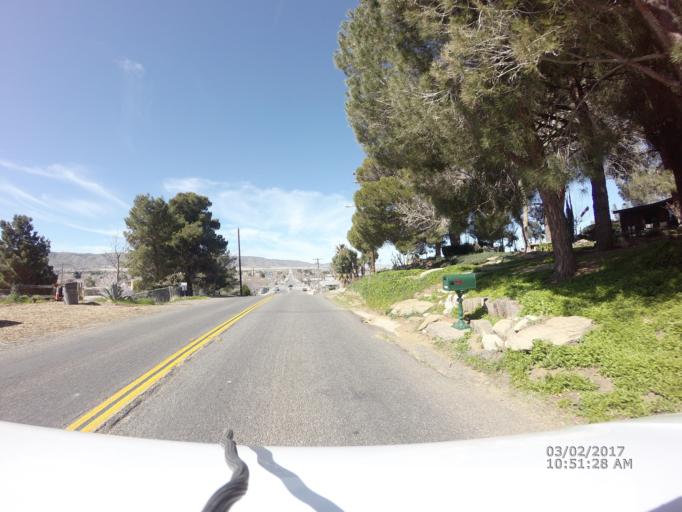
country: US
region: California
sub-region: Los Angeles County
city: Quartz Hill
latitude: 34.6456
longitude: -118.2161
